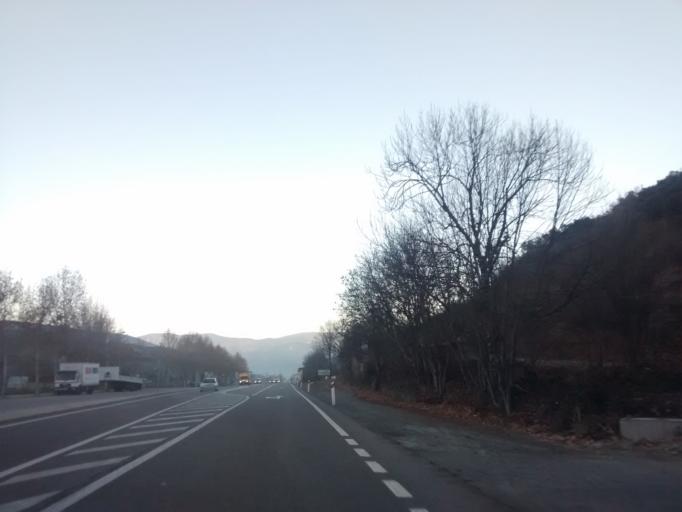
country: ES
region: Catalonia
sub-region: Provincia de Lleida
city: la Seu d'Urgell
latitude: 42.3532
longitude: 1.4383
